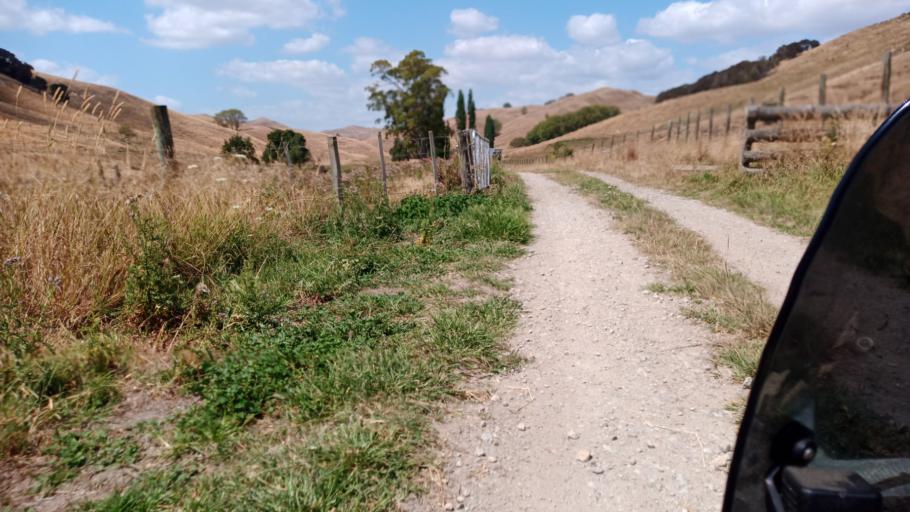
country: NZ
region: Gisborne
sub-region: Gisborne District
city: Gisborne
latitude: -38.4809
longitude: 177.8252
